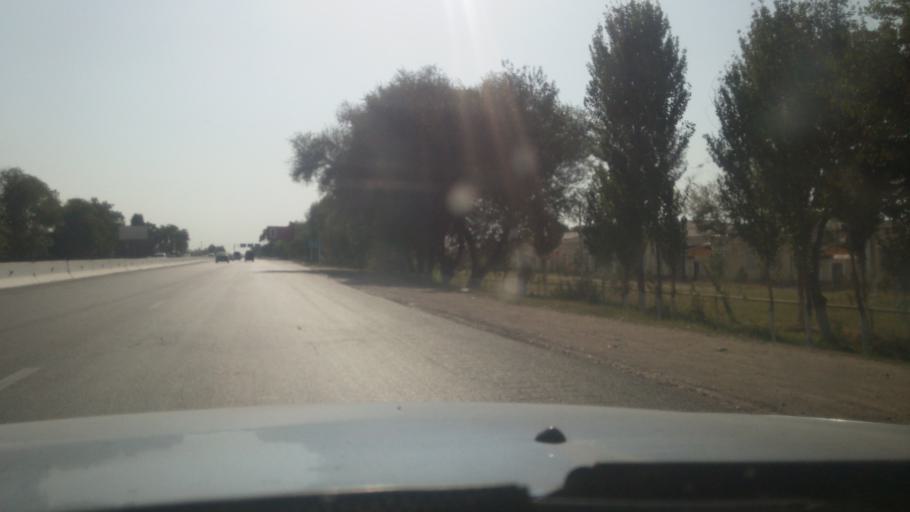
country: UZ
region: Toshkent
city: Urtaowul
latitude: 41.2252
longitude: 69.1432
